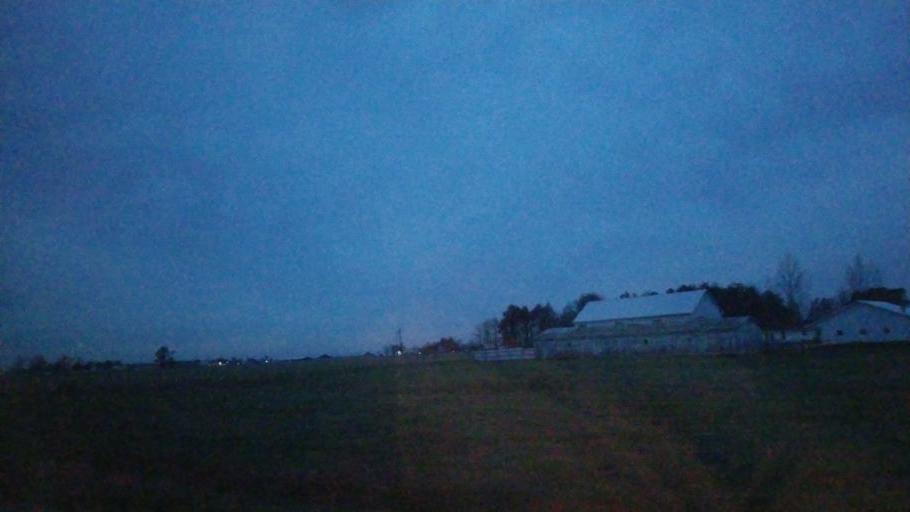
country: US
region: Indiana
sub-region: Adams County
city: Berne
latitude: 40.6941
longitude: -84.9563
